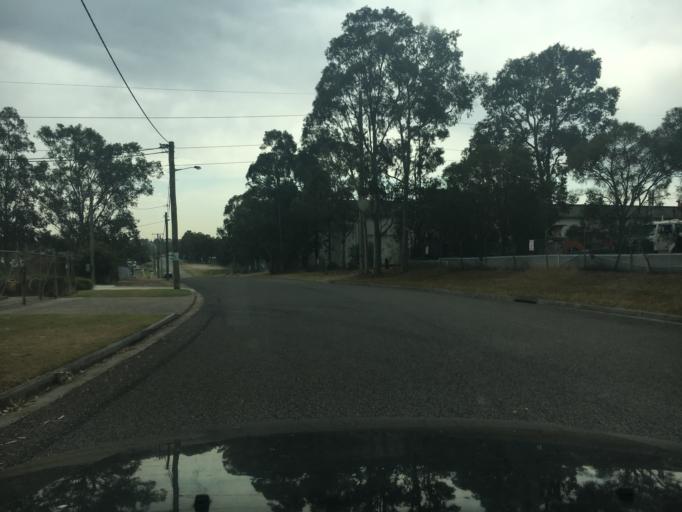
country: AU
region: New South Wales
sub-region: Maitland Municipality
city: East Maitland
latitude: -32.7614
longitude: 151.5990
